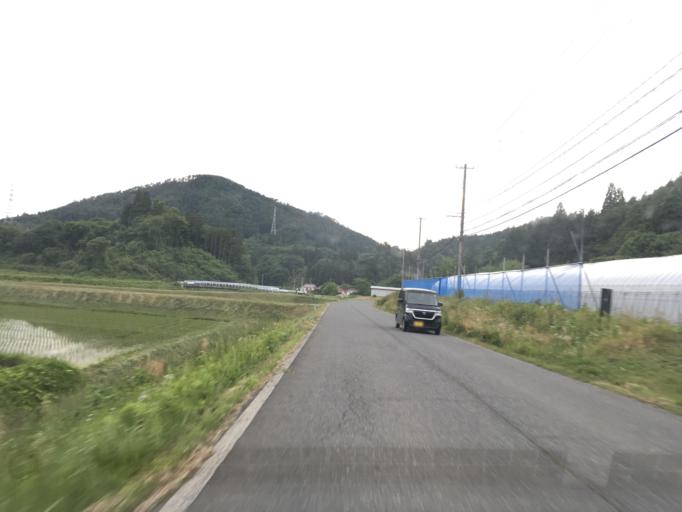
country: JP
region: Iwate
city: Mizusawa
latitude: 39.1763
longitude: 141.2935
